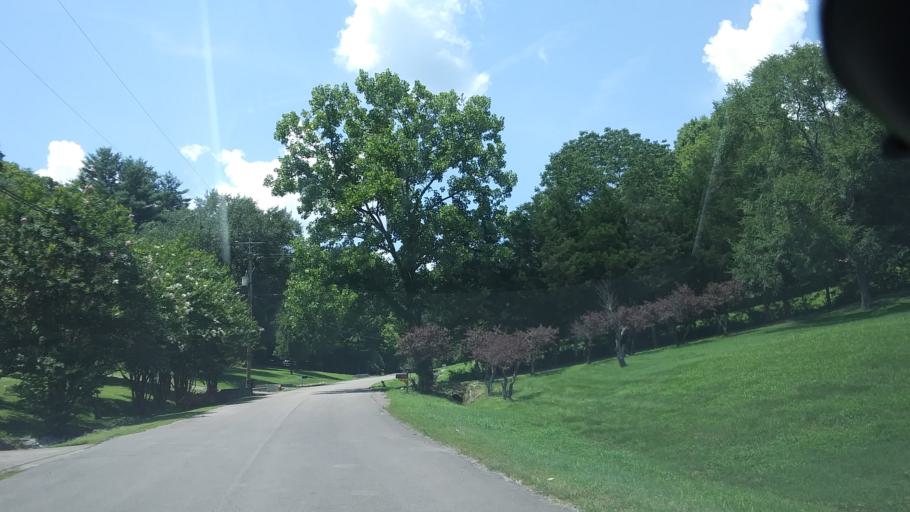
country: US
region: Tennessee
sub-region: Davidson County
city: Belle Meade
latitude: 36.1257
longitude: -86.9349
